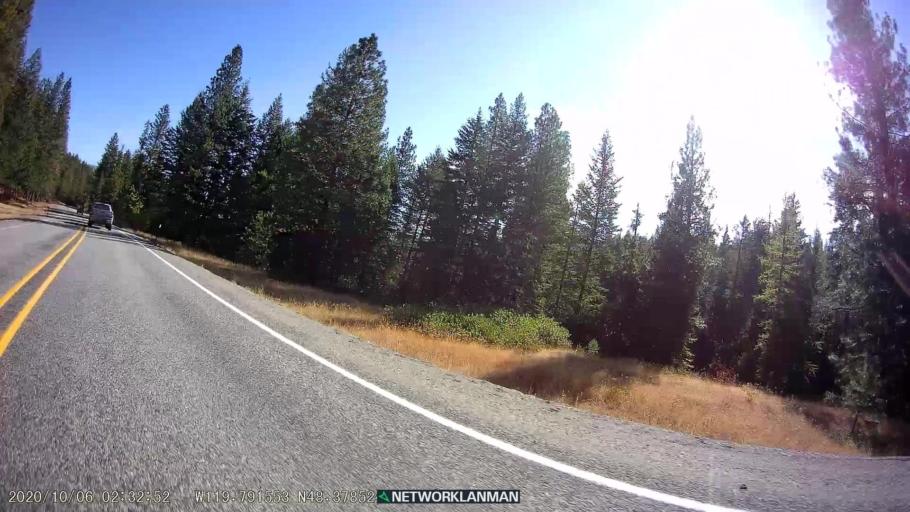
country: US
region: Washington
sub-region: Okanogan County
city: Okanogan
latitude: 48.3787
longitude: -119.7915
